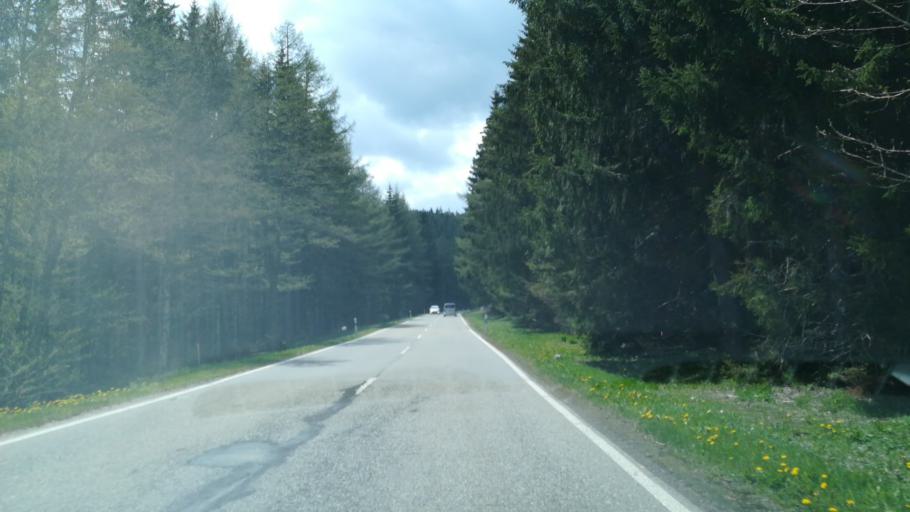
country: DE
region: Baden-Wuerttemberg
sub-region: Freiburg Region
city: Staufen
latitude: 47.7955
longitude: 8.2265
